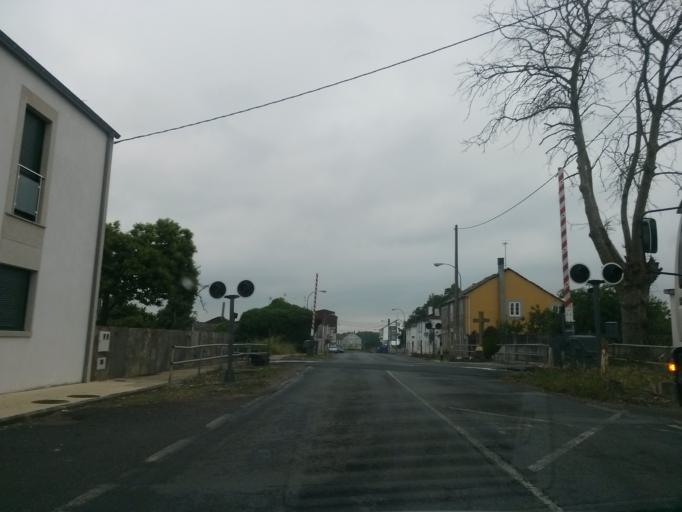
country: ES
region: Galicia
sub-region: Provincia de Lugo
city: Rabade
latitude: 43.1191
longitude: -7.6196
